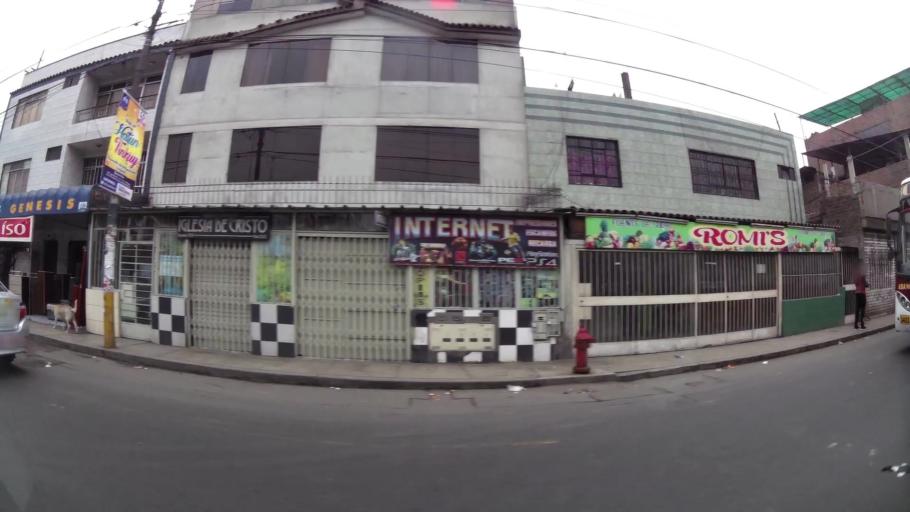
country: PE
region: Lima
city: Lima
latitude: -12.0177
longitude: -77.0122
